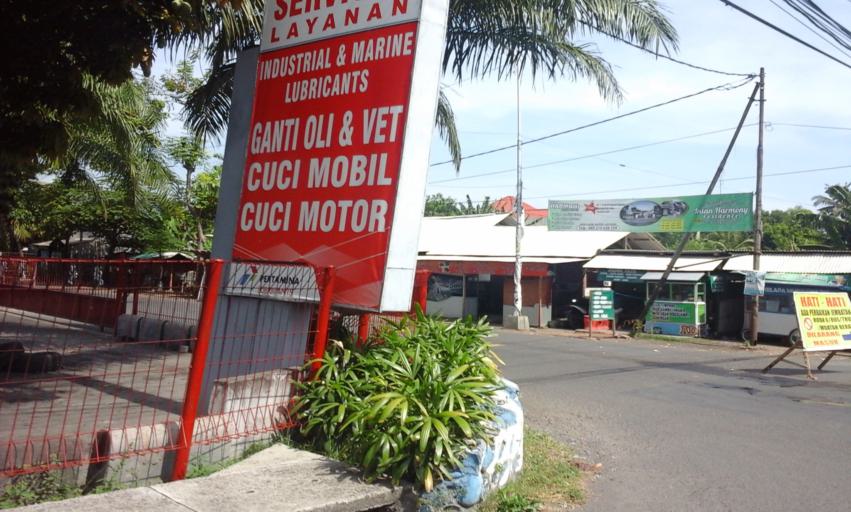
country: ID
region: East Java
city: Klatakan
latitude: -8.1519
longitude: 114.3971
